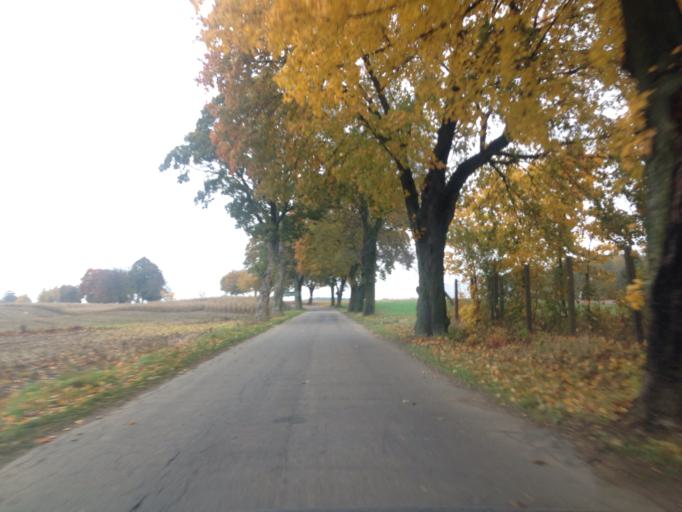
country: PL
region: Kujawsko-Pomorskie
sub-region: Powiat brodnicki
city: Brzozie
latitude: 53.2917
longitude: 19.6826
